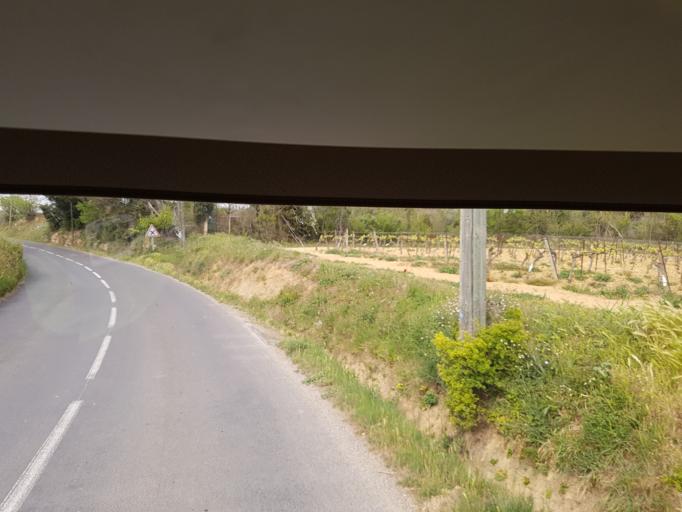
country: FR
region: Languedoc-Roussillon
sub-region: Departement de l'Aude
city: Fleury
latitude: 43.2223
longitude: 3.1321
